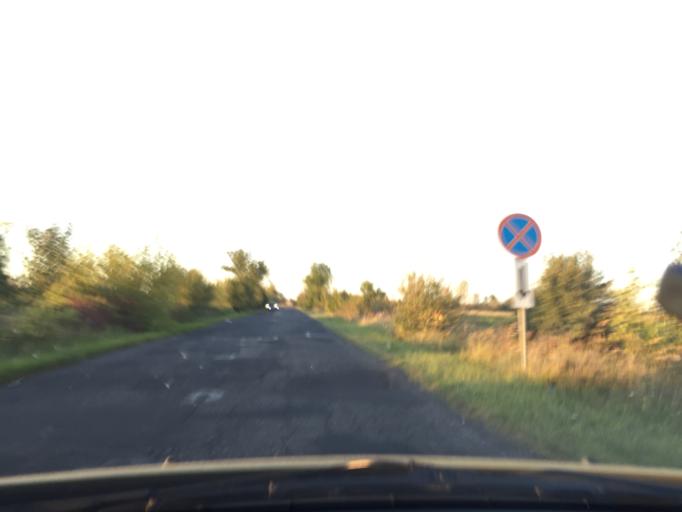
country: PL
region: Greater Poland Voivodeship
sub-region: Powiat pleszewski
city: Dobrzyca
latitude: 51.8312
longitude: 17.6200
